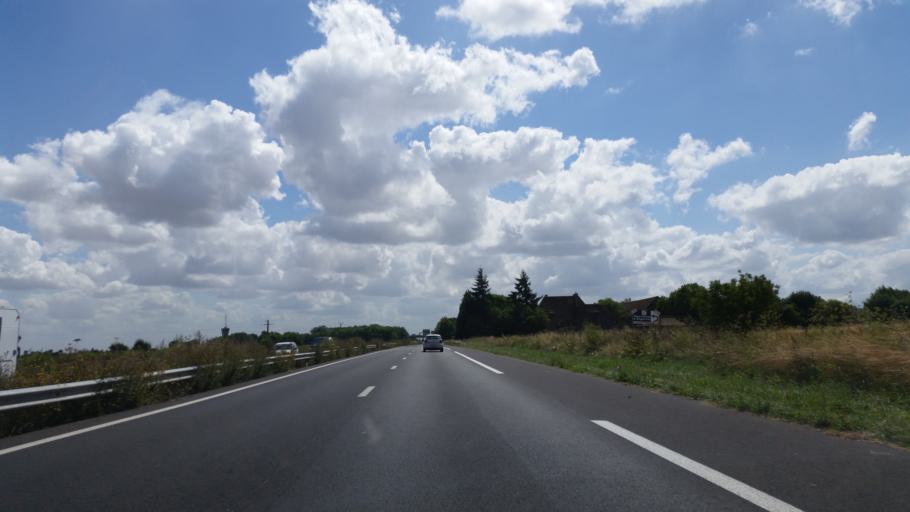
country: FR
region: Lower Normandy
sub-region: Departement du Calvados
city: Bretteville-sur-Laize
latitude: 49.0483
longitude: -0.2831
